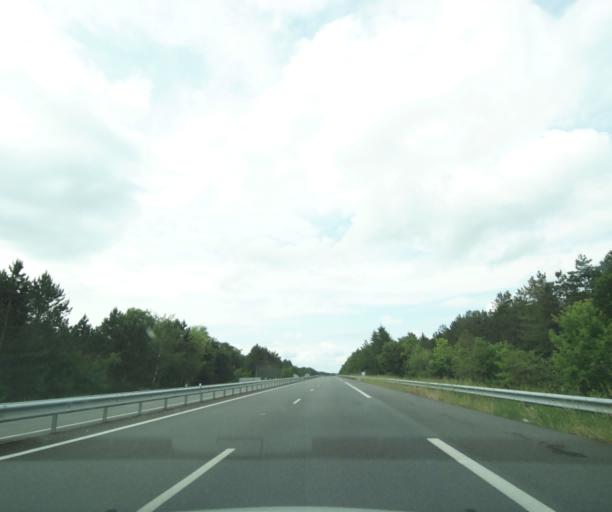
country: FR
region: Centre
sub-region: Departement du Cher
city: Levet
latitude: 46.8728
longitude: 2.4249
